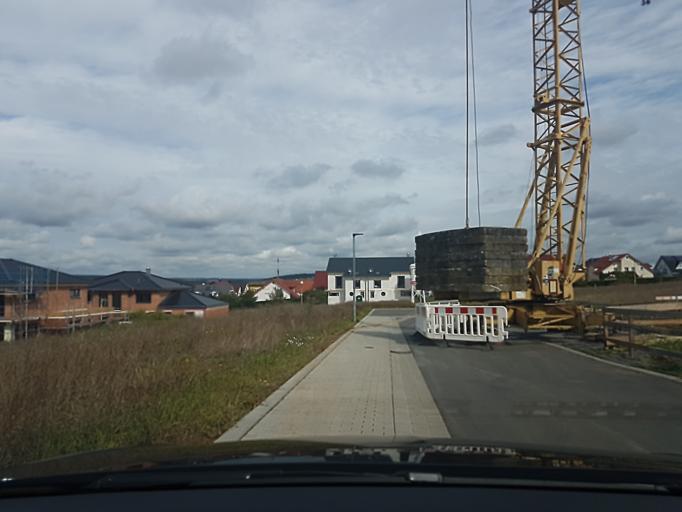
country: DE
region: Baden-Wuerttemberg
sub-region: Regierungsbezirk Stuttgart
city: Mockmuhl
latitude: 49.3123
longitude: 9.3691
